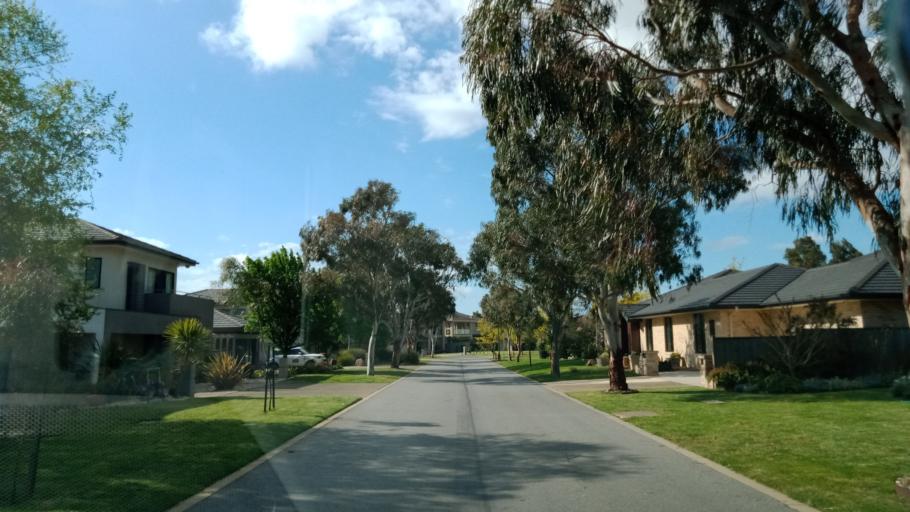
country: AU
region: Victoria
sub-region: Frankston
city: Sandhurst
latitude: -38.0804
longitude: 145.2170
